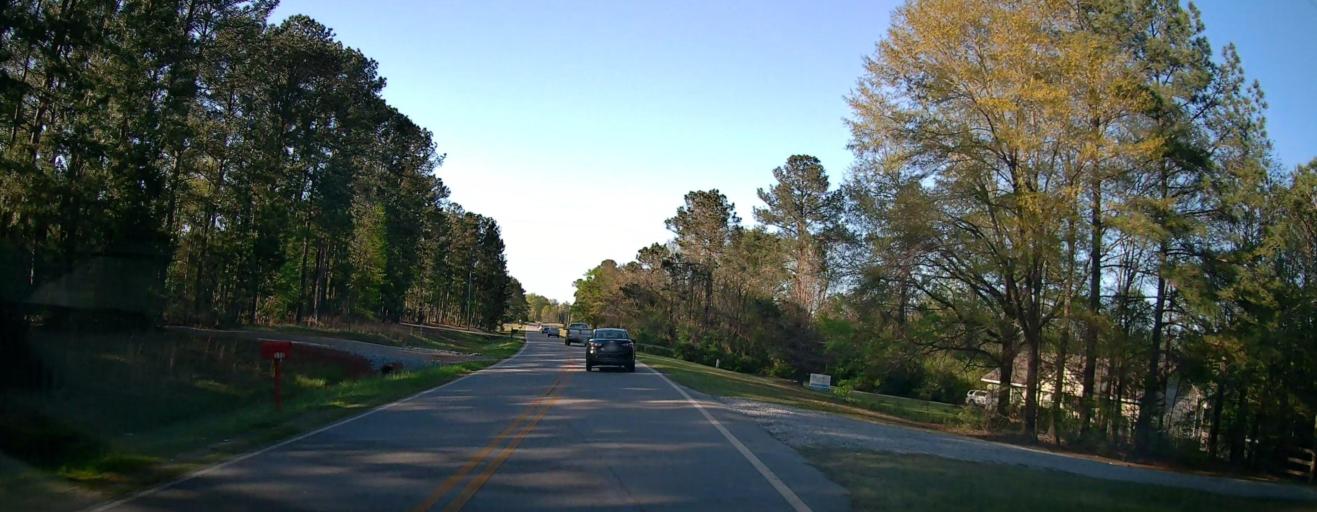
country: US
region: Georgia
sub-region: Butts County
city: Indian Springs
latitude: 33.2782
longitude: -83.8967
